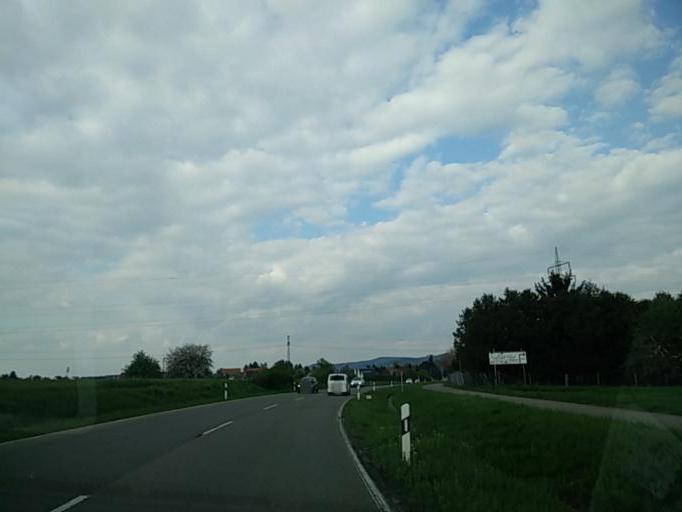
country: DE
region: Baden-Wuerttemberg
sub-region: Tuebingen Region
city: Nehren
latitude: 48.4216
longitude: 9.0576
